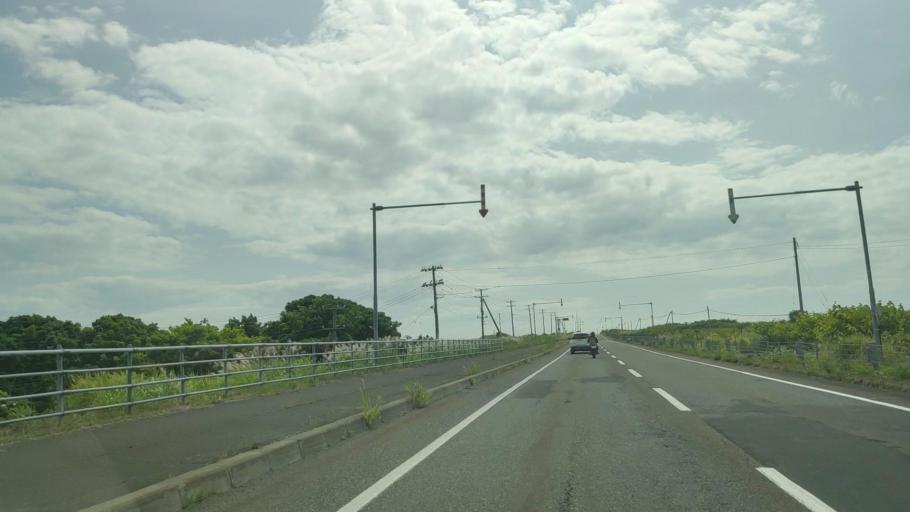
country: JP
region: Hokkaido
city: Rumoi
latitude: 44.4457
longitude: 141.7560
